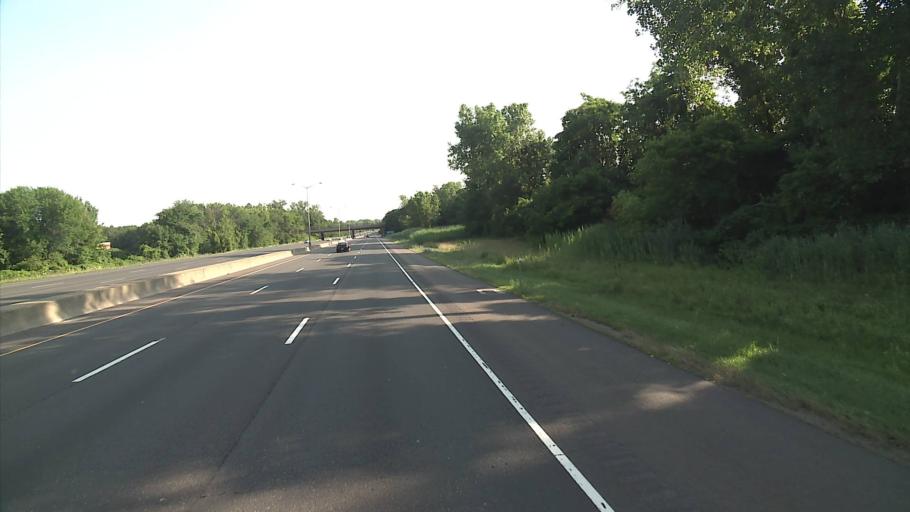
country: US
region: Connecticut
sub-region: Hartford County
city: Windsor Locks
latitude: 41.9408
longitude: -72.6066
